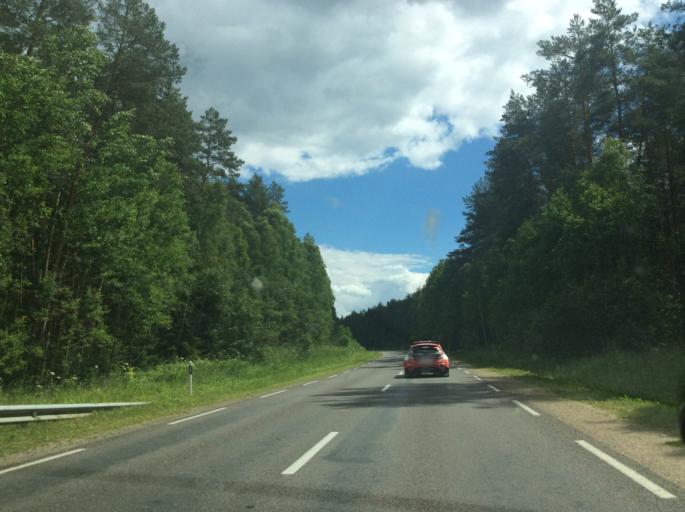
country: LT
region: Alytaus apskritis
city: Druskininkai
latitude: 54.0385
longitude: 23.9501
